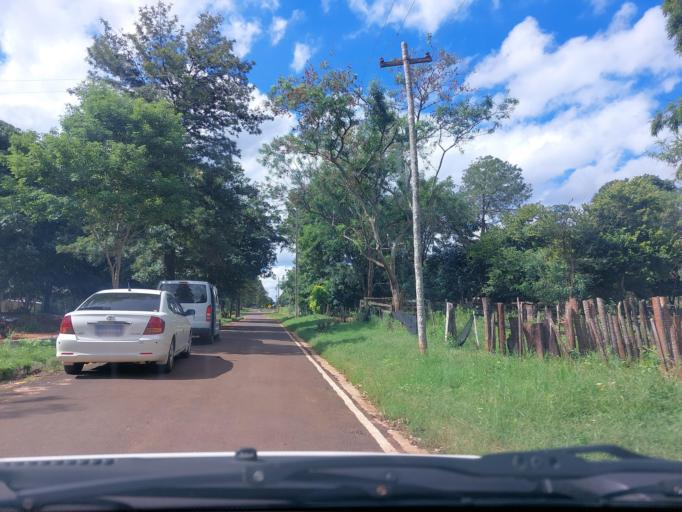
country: PY
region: San Pedro
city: Guayaybi
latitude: -24.5314
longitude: -56.5588
